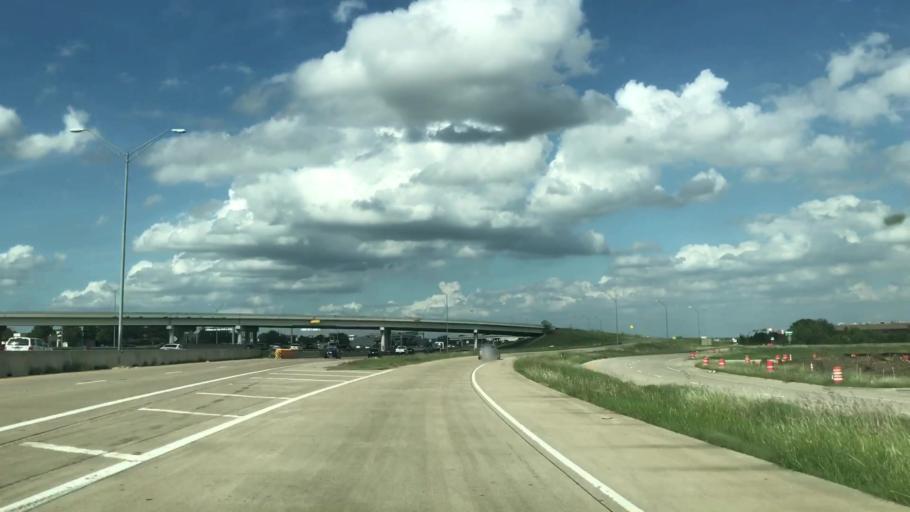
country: US
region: Texas
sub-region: Dallas County
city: Coppell
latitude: 32.9597
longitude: -97.0394
